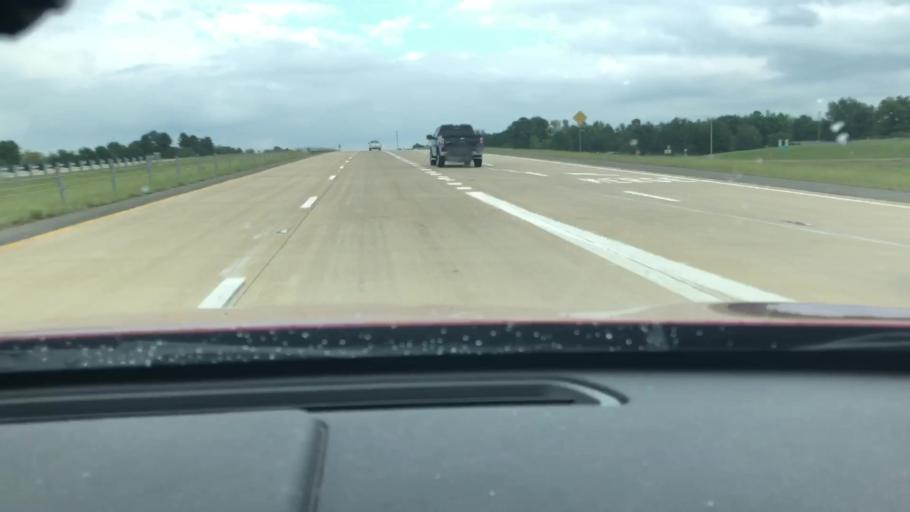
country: US
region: Texas
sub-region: Bowie County
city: Texarkana
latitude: 33.3917
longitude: -94.0149
